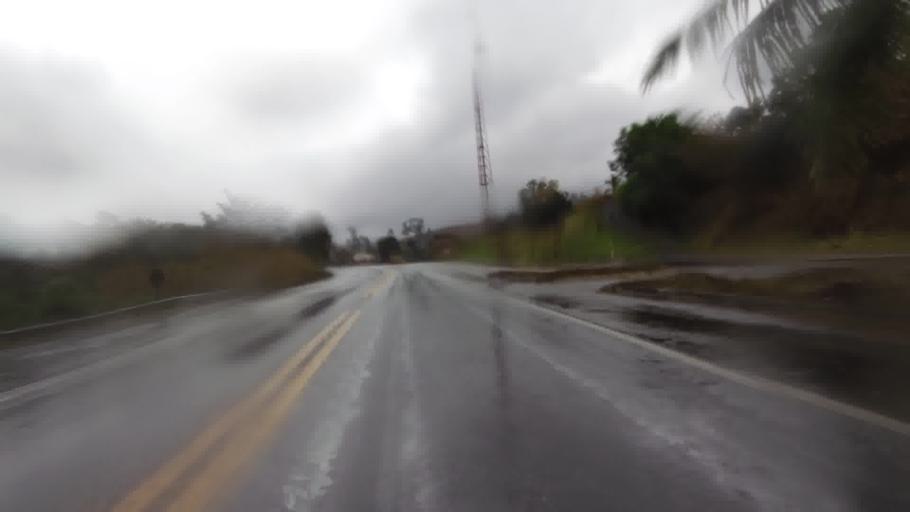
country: BR
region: Espirito Santo
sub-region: Cachoeiro De Itapemirim
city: Cachoeiro de Itapemirim
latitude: -20.9201
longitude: -41.0767
